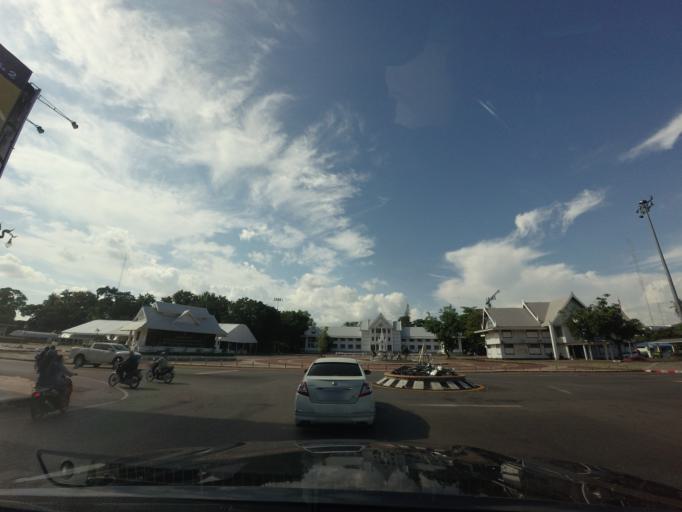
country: TH
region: Nong Khai
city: Nong Khai
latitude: 17.8787
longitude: 102.7410
